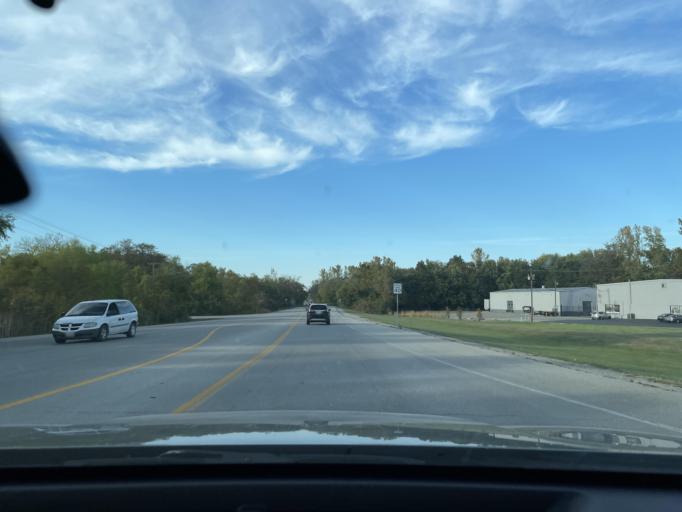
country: US
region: Missouri
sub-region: Andrew County
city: Country Club Village
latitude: 39.7831
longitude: -94.7675
